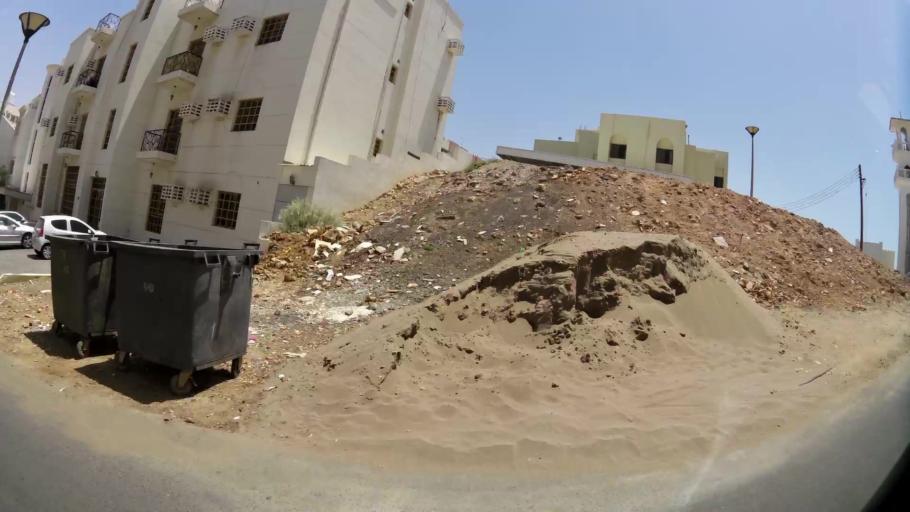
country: OM
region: Muhafazat Masqat
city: Muscat
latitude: 23.6200
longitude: 58.4988
